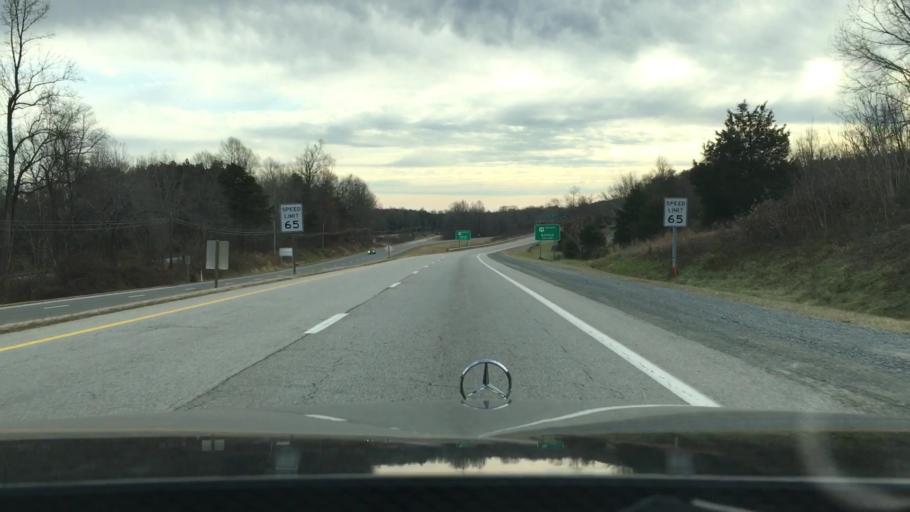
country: US
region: Virginia
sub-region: Pittsylvania County
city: Gretna
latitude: 36.9833
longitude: -79.3546
